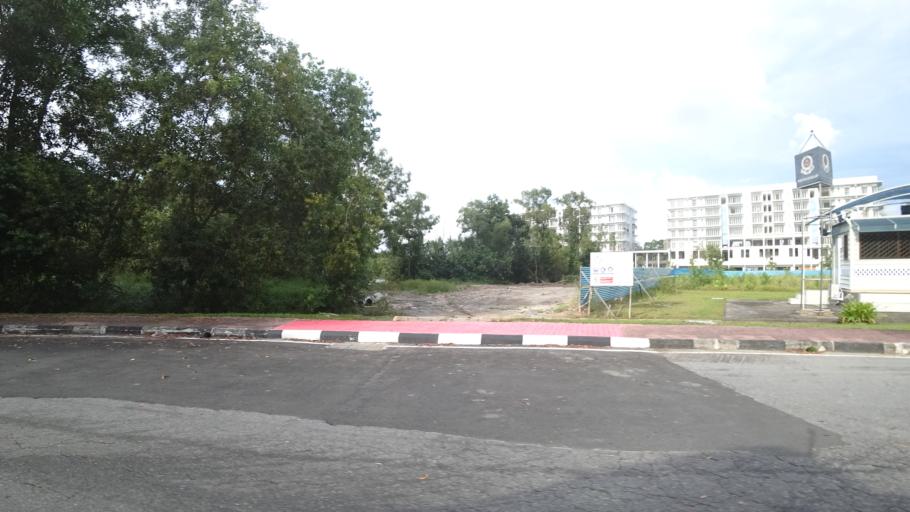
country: BN
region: Brunei and Muara
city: Bandar Seri Begawan
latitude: 4.9050
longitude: 114.9270
